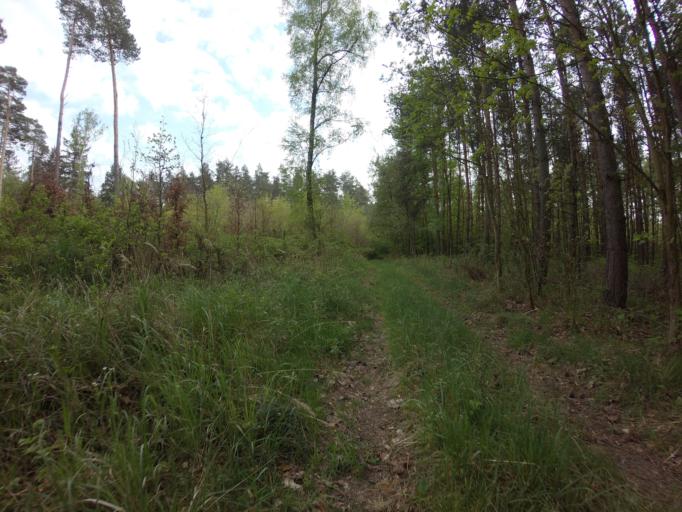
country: PL
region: West Pomeranian Voivodeship
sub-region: Powiat choszczenski
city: Choszczno
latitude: 53.1551
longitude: 15.3235
